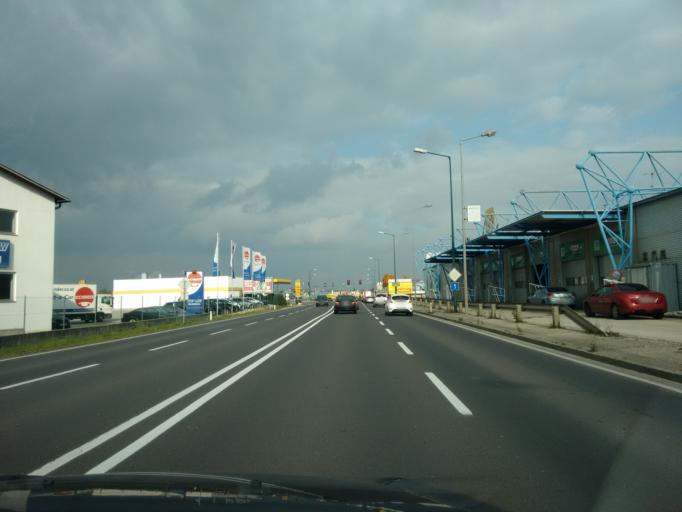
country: AT
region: Upper Austria
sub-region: Wels-Land
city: Gunskirchen
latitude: 48.1475
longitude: 13.9760
